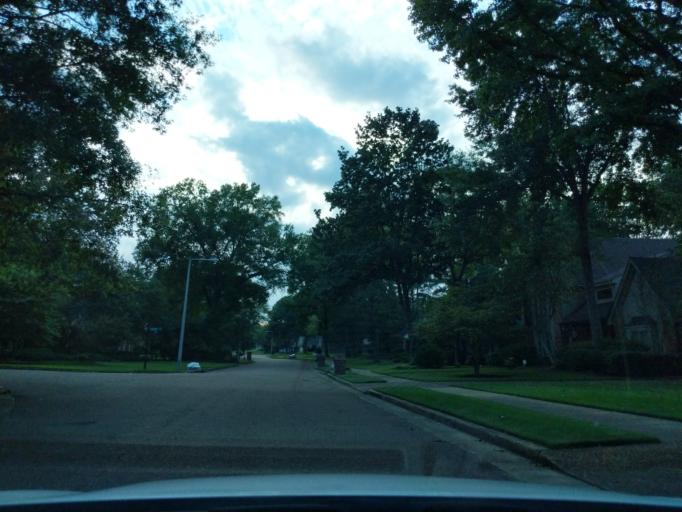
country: US
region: Tennessee
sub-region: Shelby County
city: Germantown
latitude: 35.0668
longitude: -89.7814
